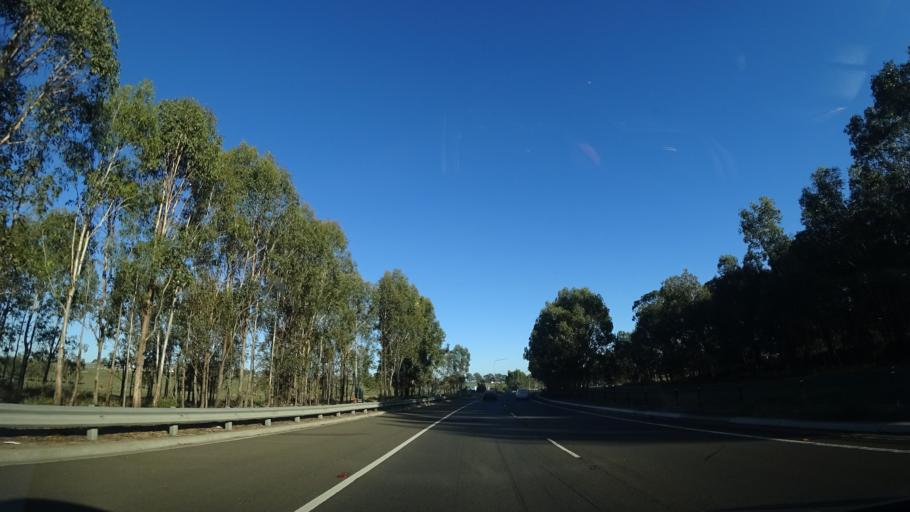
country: AU
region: New South Wales
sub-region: Blacktown
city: Rouse Hill
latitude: -33.6707
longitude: 150.9033
